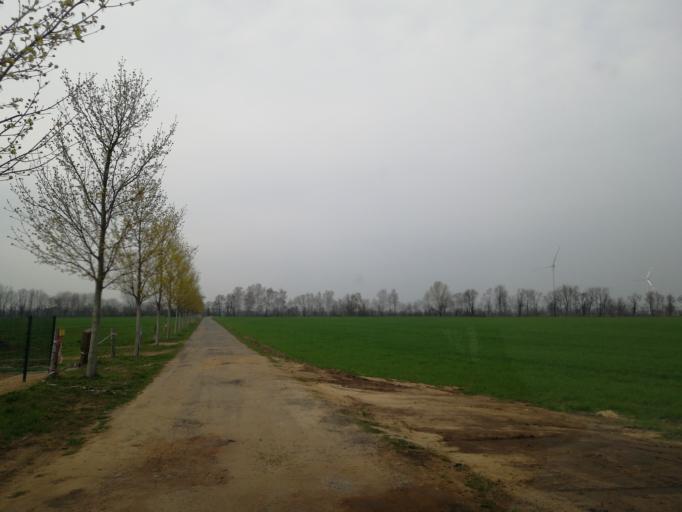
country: DE
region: Brandenburg
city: Elsterwerda
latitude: 51.4299
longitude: 13.4877
